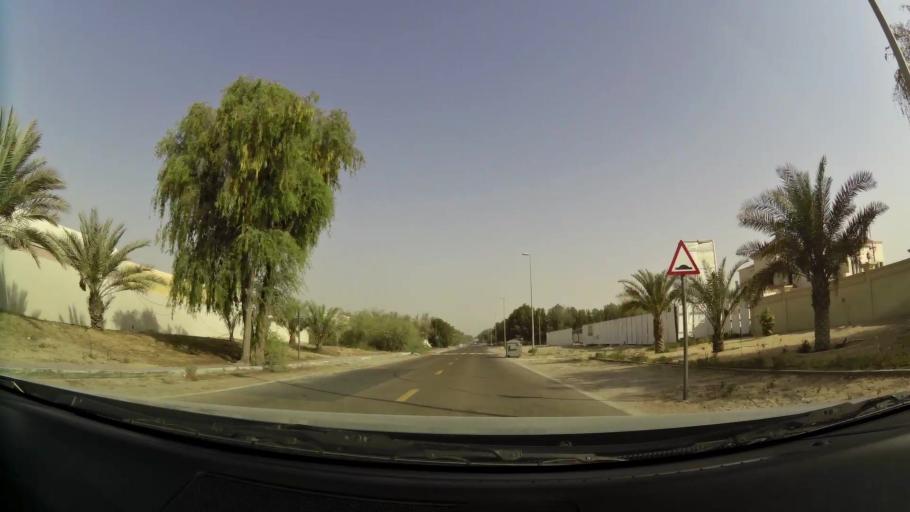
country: AE
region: Dubai
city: Dubai
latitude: 25.1521
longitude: 55.3195
